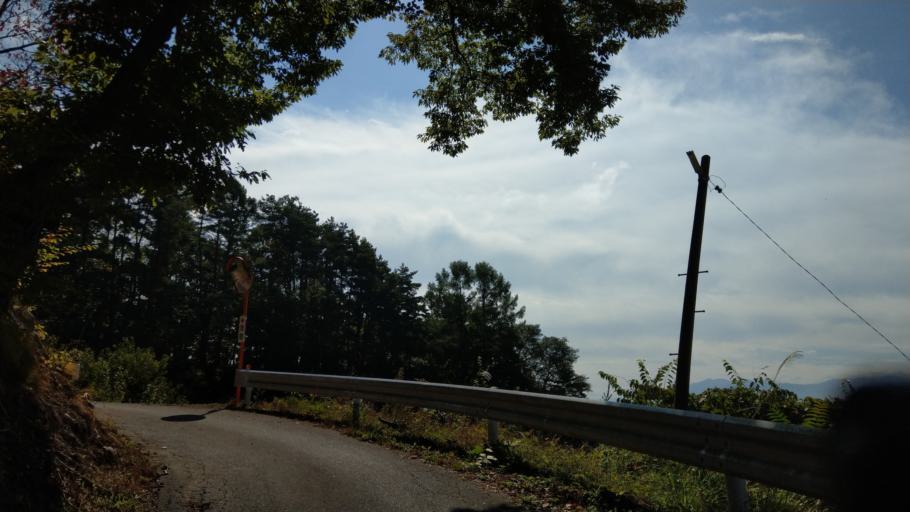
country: JP
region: Nagano
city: Komoro
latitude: 36.3579
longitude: 138.4317
